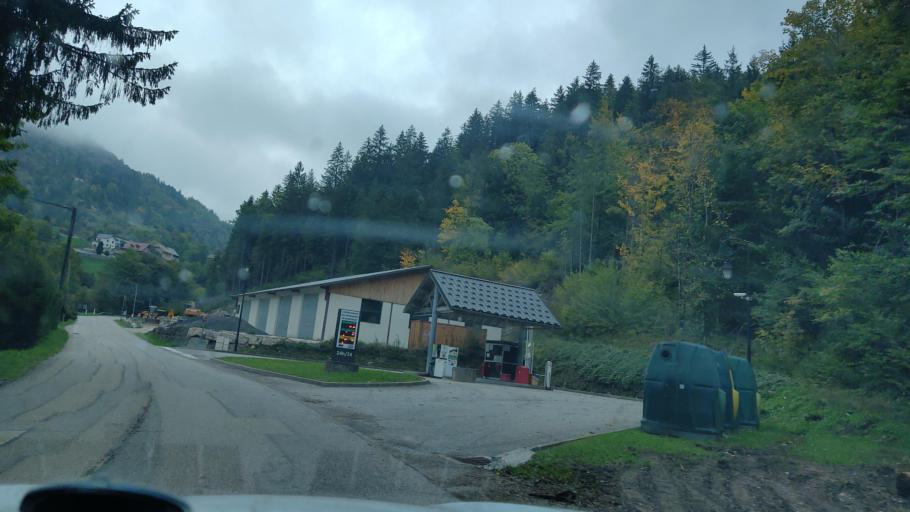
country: FR
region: Rhone-Alpes
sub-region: Departement de l'Isere
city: Saint-Vincent-de-Mercuze
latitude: 45.4213
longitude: 5.8611
